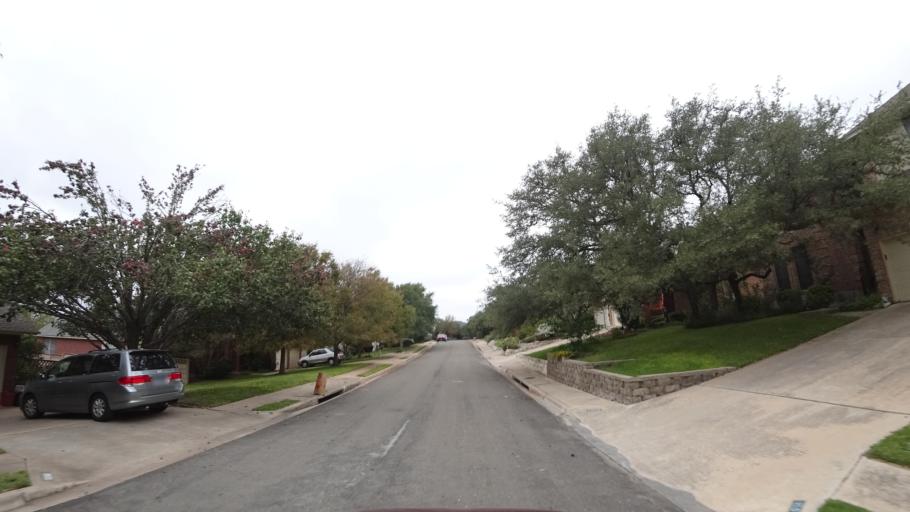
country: US
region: Texas
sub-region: Williamson County
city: Anderson Mill
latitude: 30.4353
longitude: -97.8260
